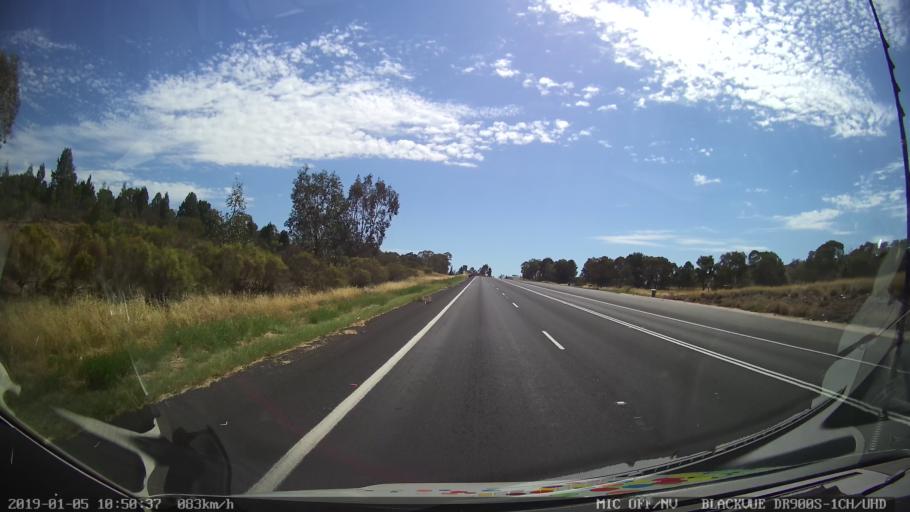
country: AU
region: New South Wales
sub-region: Warrumbungle Shire
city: Coonabarabran
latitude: -31.4279
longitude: 149.0778
